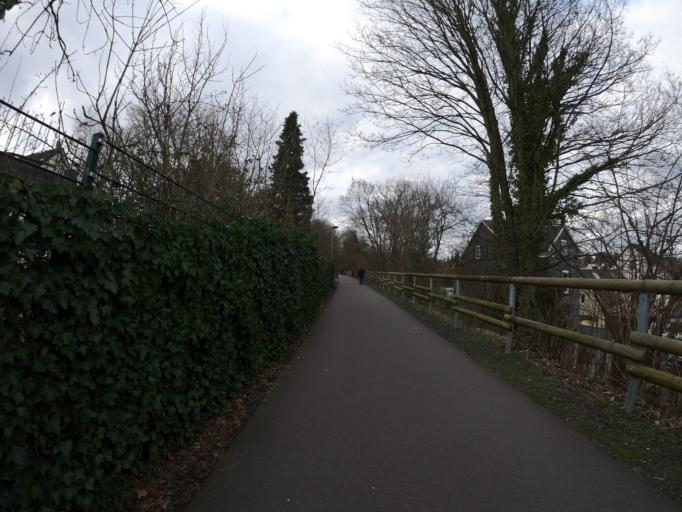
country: DE
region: North Rhine-Westphalia
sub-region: Regierungsbezirk Dusseldorf
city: Solingen
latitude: 51.1747
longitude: 7.0917
